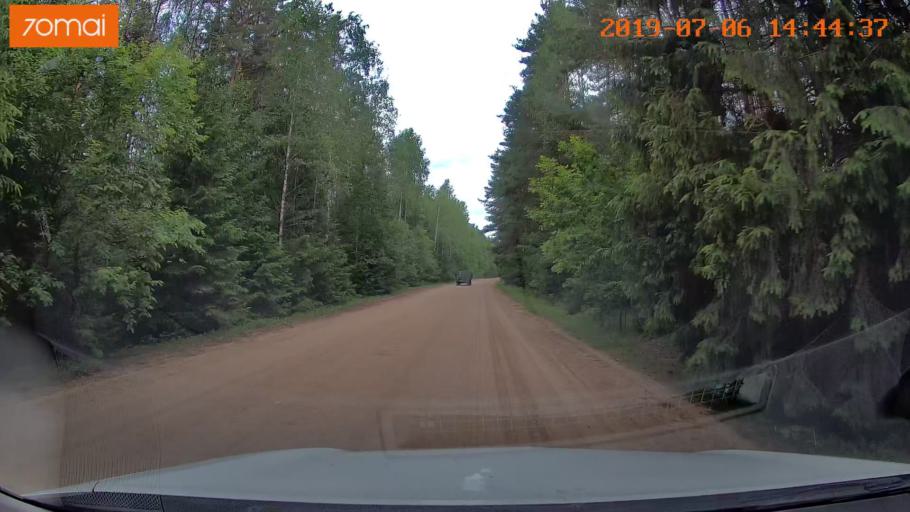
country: BY
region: Minsk
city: Ivyanyets
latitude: 53.9637
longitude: 26.6927
